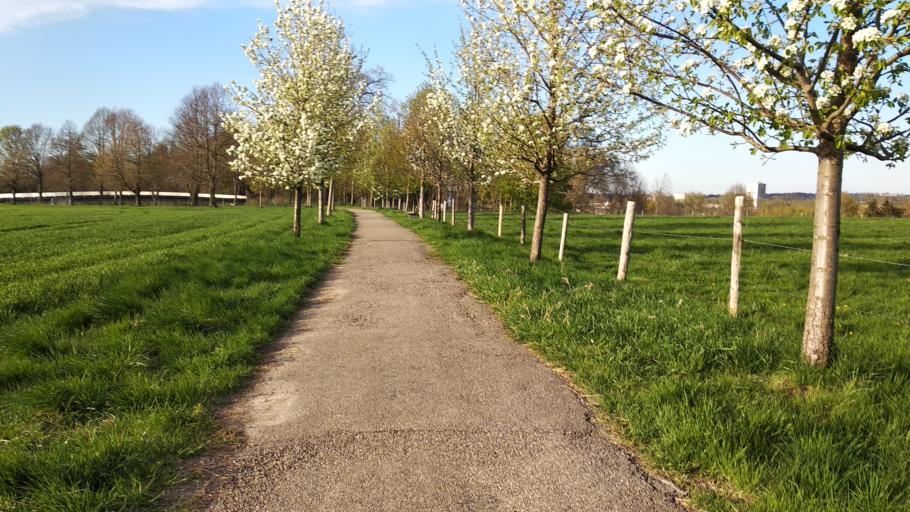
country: DE
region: Bavaria
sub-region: Swabia
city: Memmingen
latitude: 47.9636
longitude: 10.1808
